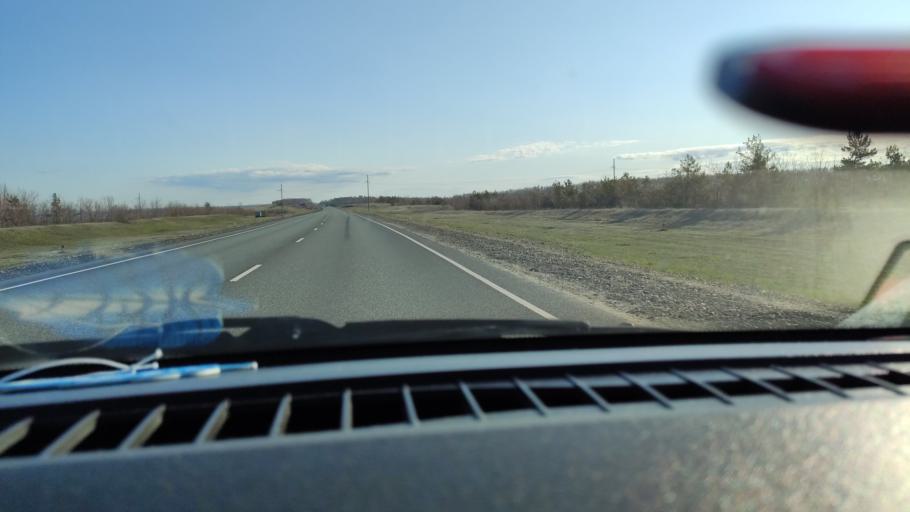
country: RU
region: Saratov
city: Khvalynsk
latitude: 52.5465
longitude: 48.0685
